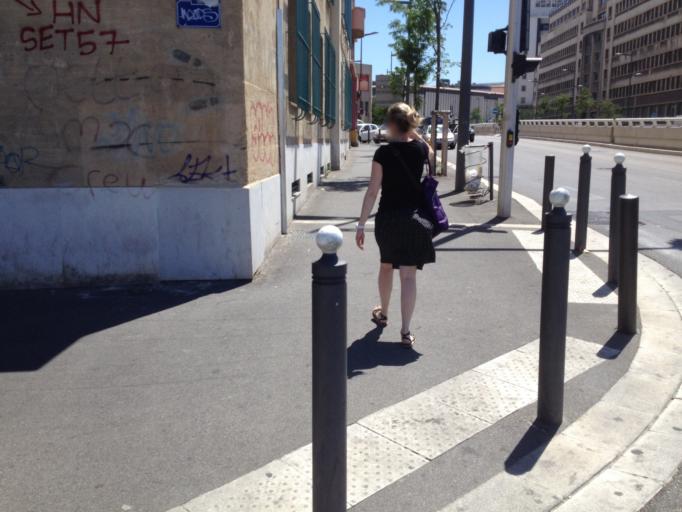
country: FR
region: Provence-Alpes-Cote d'Azur
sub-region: Departement des Bouches-du-Rhone
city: Marseille 03
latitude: 43.3047
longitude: 5.3753
